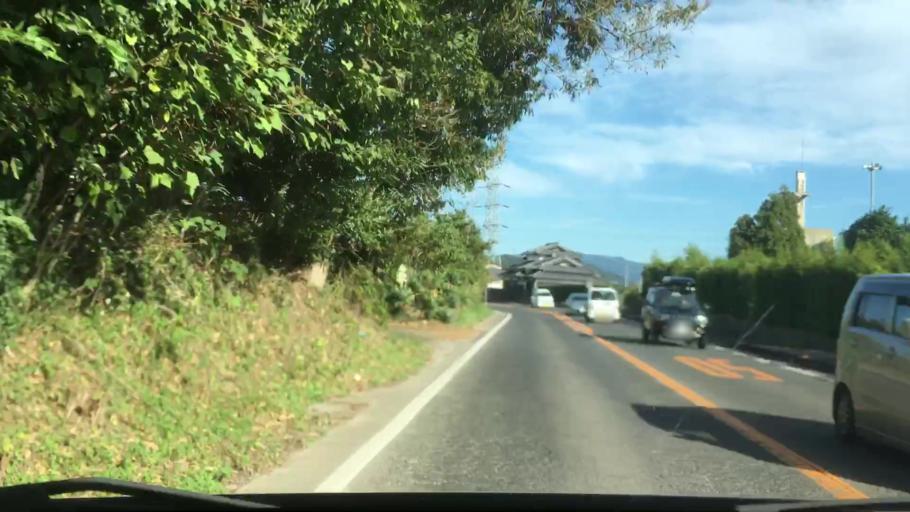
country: JP
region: Nagasaki
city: Sasebo
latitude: 33.0731
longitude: 129.7606
